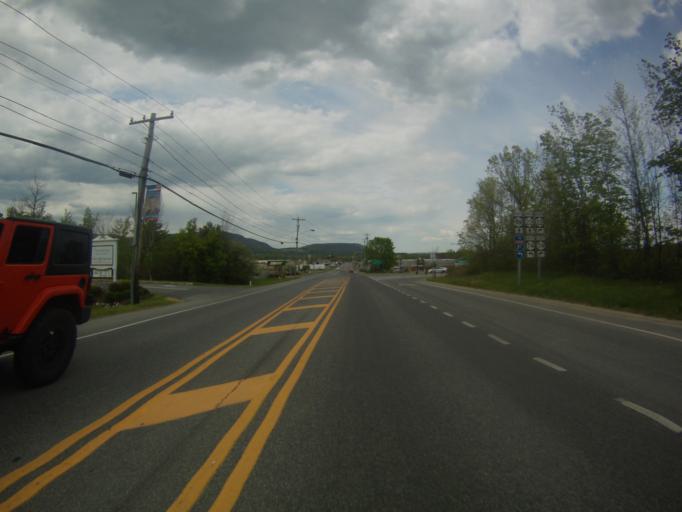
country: US
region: New York
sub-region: Essex County
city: Ticonderoga
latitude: 43.8562
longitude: -73.4382
